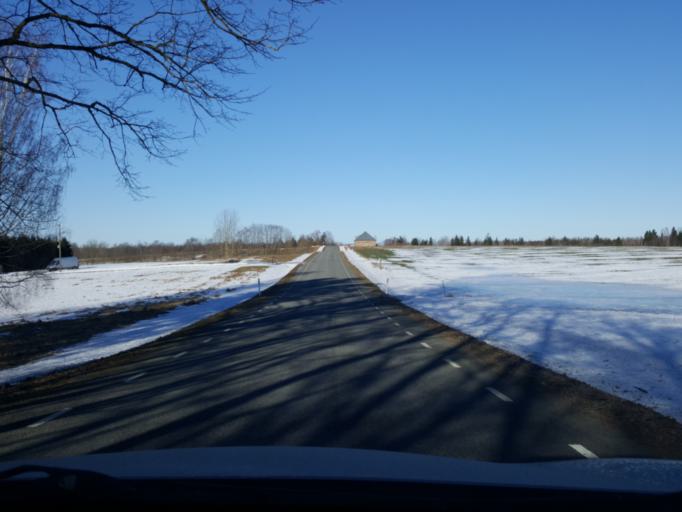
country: EE
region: Viljandimaa
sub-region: Viljandi linn
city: Viljandi
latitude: 58.4132
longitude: 25.5532
